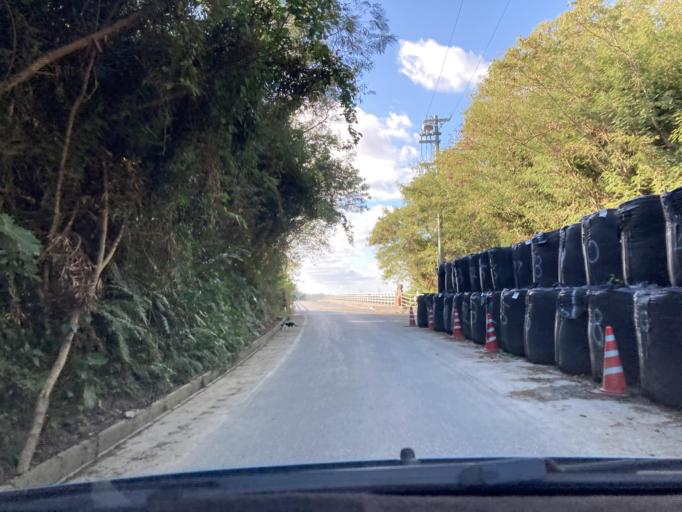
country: JP
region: Okinawa
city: Katsuren-haebaru
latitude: 26.3212
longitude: 127.9180
